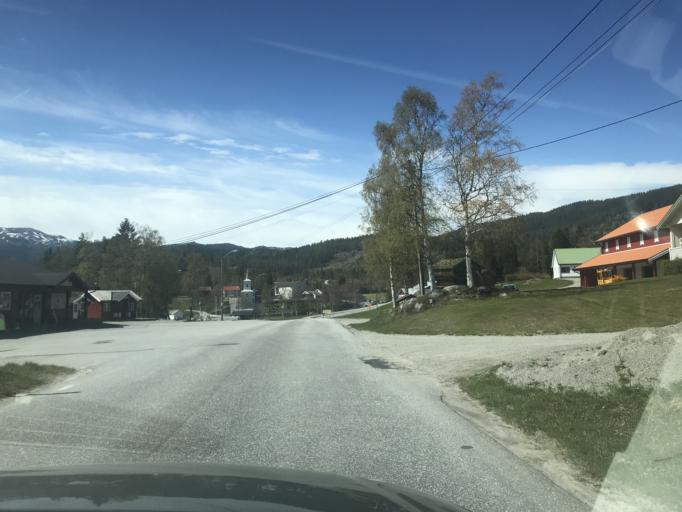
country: NO
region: Telemark
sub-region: Hjartdal
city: Sauland
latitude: 59.7550
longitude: 8.7932
